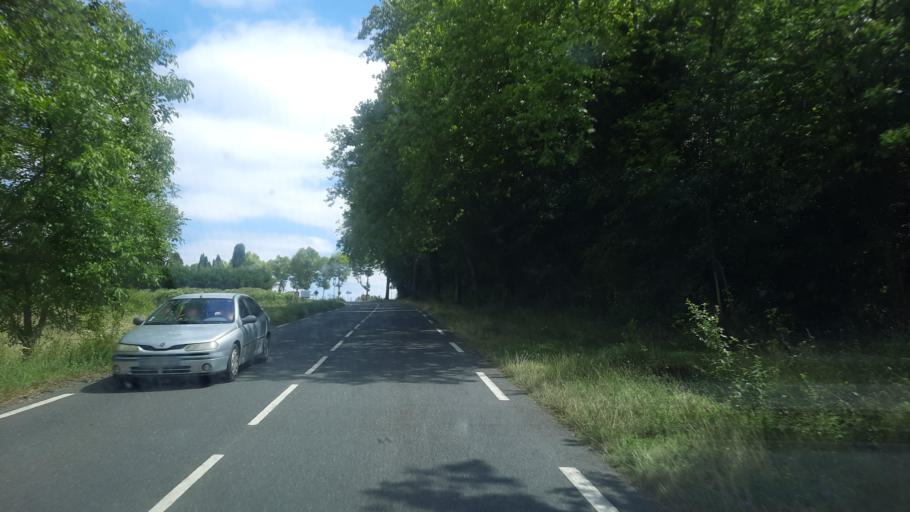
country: FR
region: Midi-Pyrenees
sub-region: Departement de la Haute-Garonne
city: Boulogne-sur-Gesse
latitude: 43.2896
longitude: 0.6374
